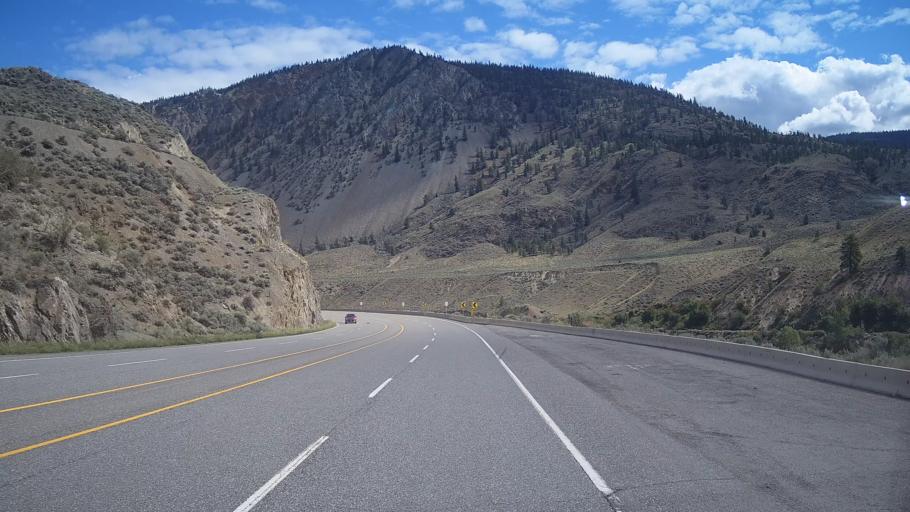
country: CA
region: British Columbia
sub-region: Thompson-Nicola Regional District
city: Ashcroft
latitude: 50.5098
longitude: -121.2840
